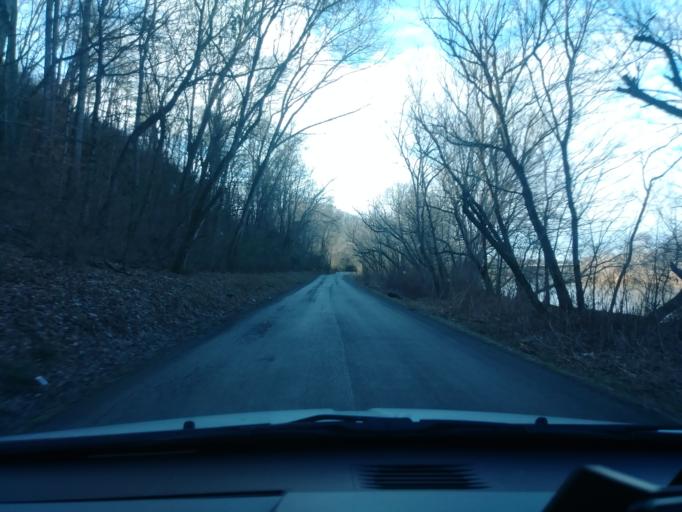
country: US
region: Tennessee
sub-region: Cocke County
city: Newport
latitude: 35.9795
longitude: -83.1567
